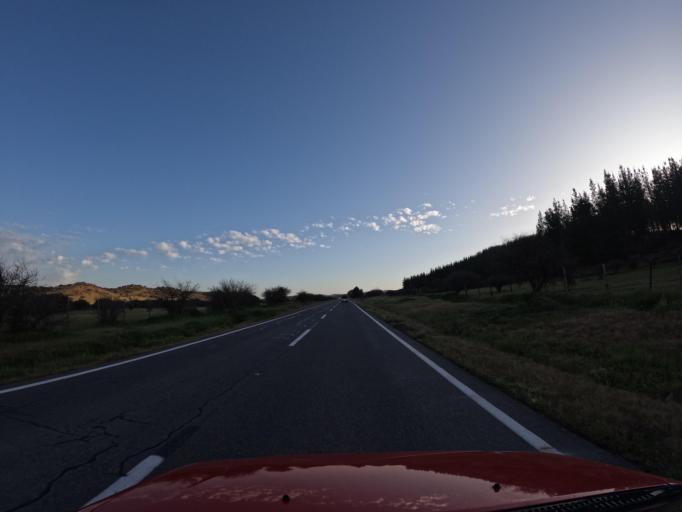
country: CL
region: O'Higgins
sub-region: Provincia de Colchagua
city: Santa Cruz
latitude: -34.2988
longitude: -71.7331
